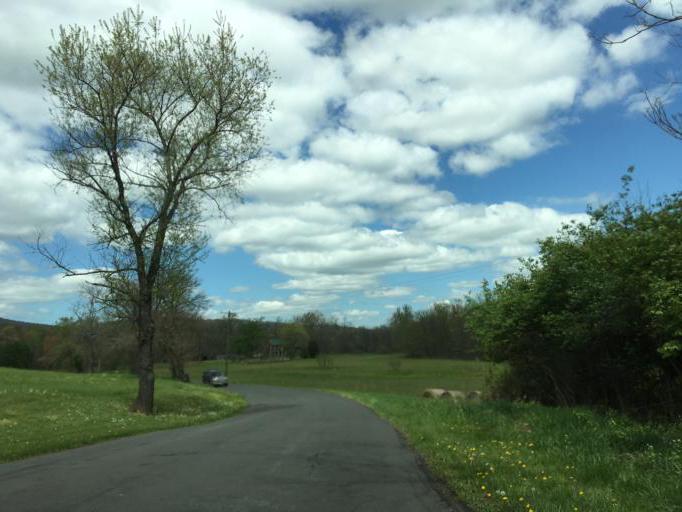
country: US
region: Maryland
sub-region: Frederick County
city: Thurmont
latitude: 39.6374
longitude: -77.3961
